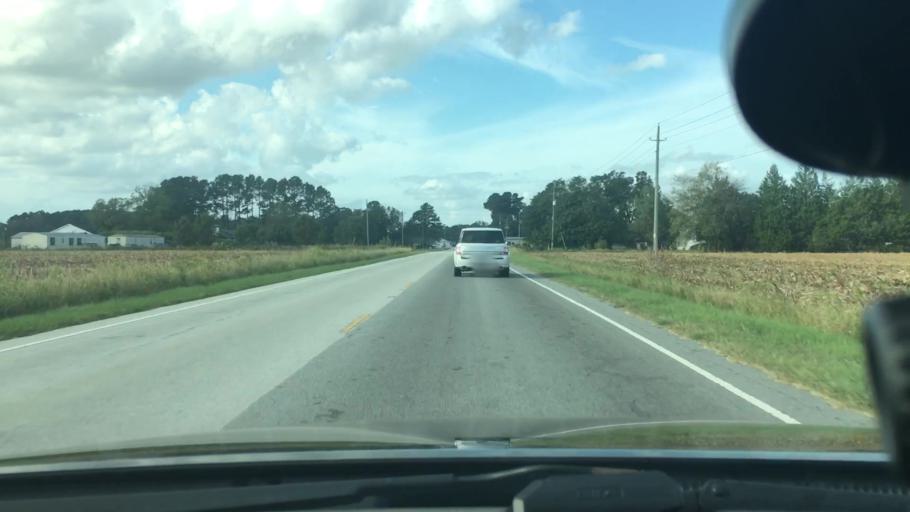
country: US
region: North Carolina
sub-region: Pitt County
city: Windsor
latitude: 35.5034
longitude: -77.3137
